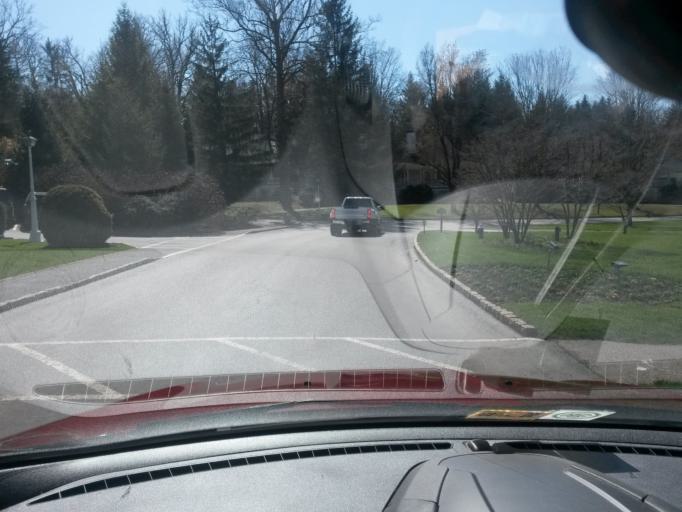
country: US
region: West Virginia
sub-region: Greenbrier County
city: White Sulphur Springs
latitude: 37.7872
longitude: -80.3095
